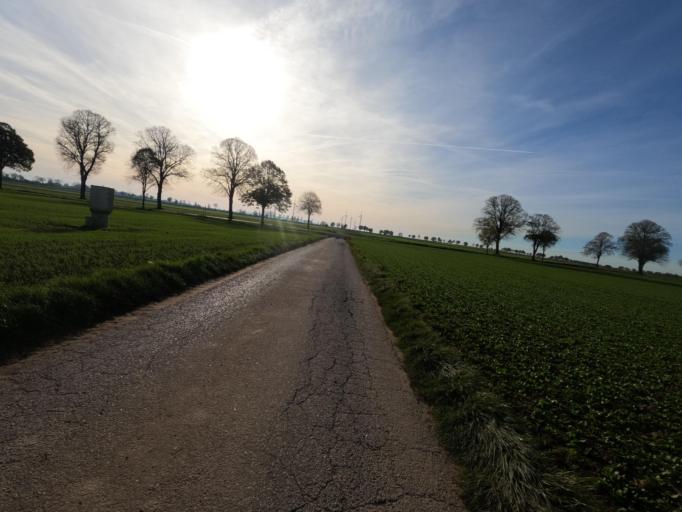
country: DE
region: North Rhine-Westphalia
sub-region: Regierungsbezirk Koln
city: Titz
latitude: 51.0492
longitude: 6.4215
